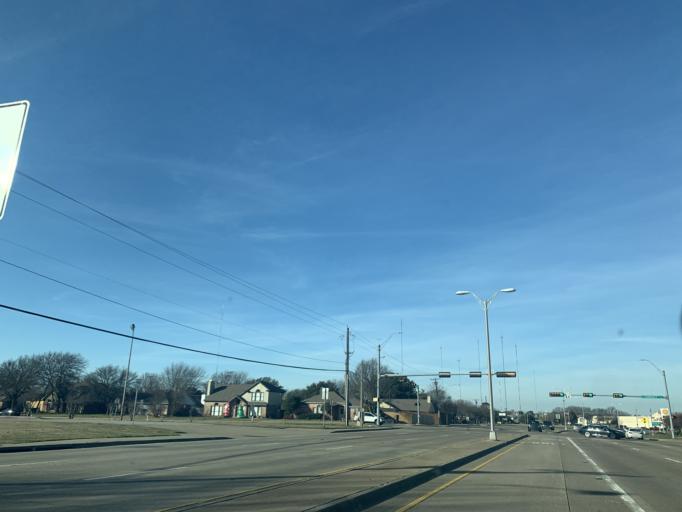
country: US
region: Texas
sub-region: Dallas County
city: Cedar Hill
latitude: 32.5899
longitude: -96.9327
